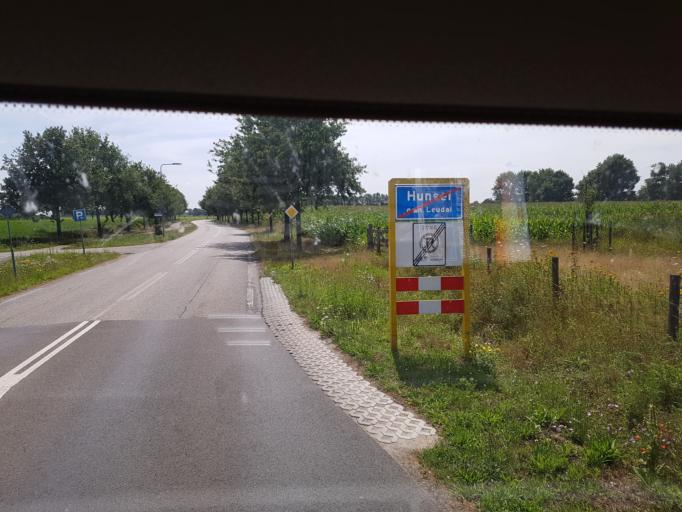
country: NL
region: Limburg
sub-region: Gemeente Leudal
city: Kelpen-Oler
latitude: 51.1869
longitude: 5.8156
